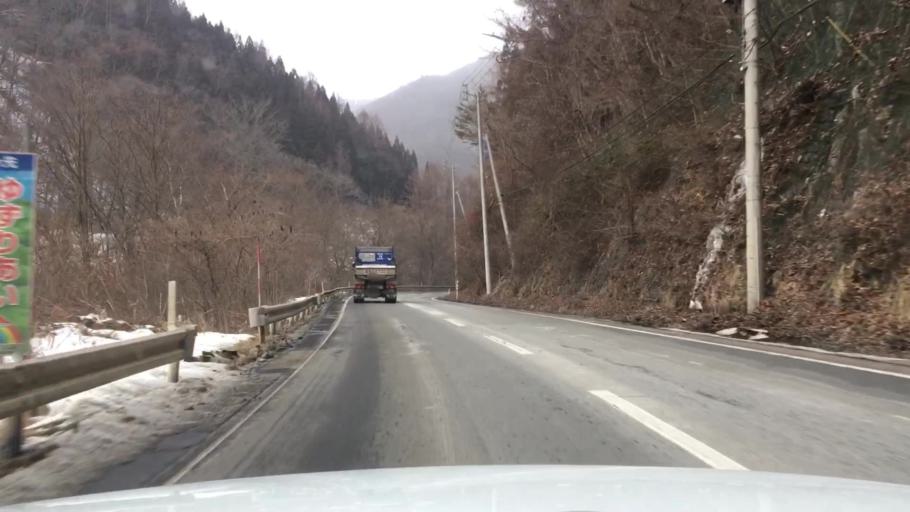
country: JP
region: Iwate
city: Tono
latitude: 39.6186
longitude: 141.4763
